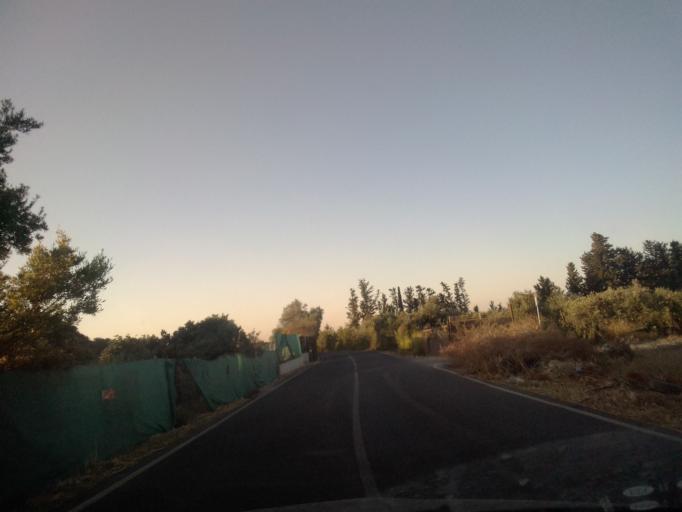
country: CY
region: Limassol
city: Ypsonas
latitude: 34.6707
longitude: 32.9600
